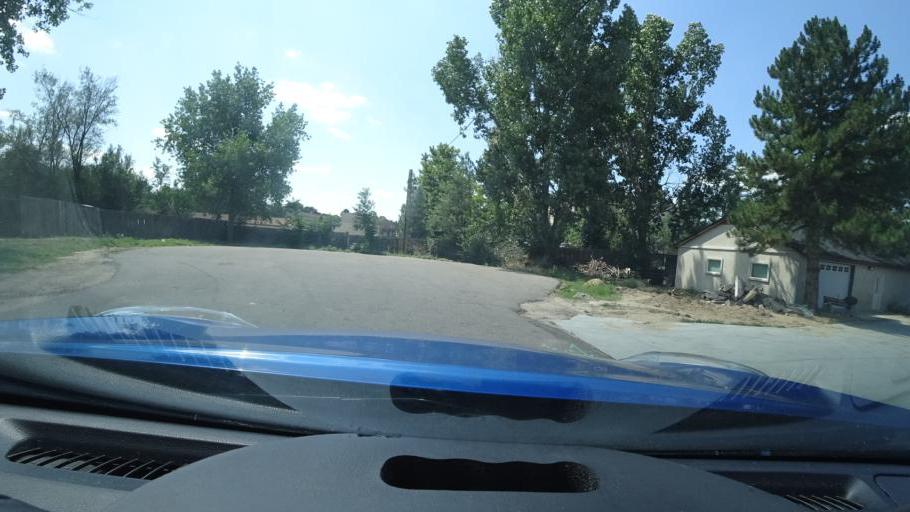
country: US
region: Colorado
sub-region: Arapahoe County
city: Glendale
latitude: 39.6933
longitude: -104.8858
